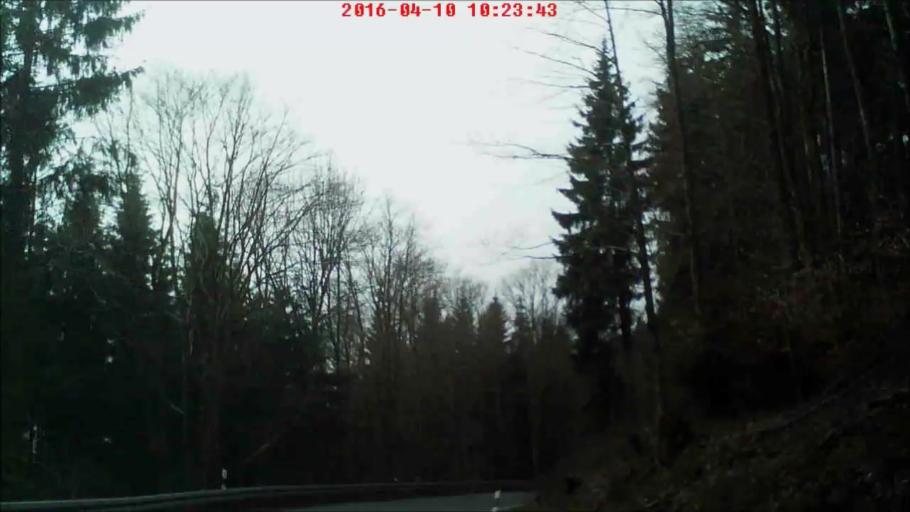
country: DE
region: Thuringia
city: Stutzerbach
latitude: 50.6561
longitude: 10.8888
